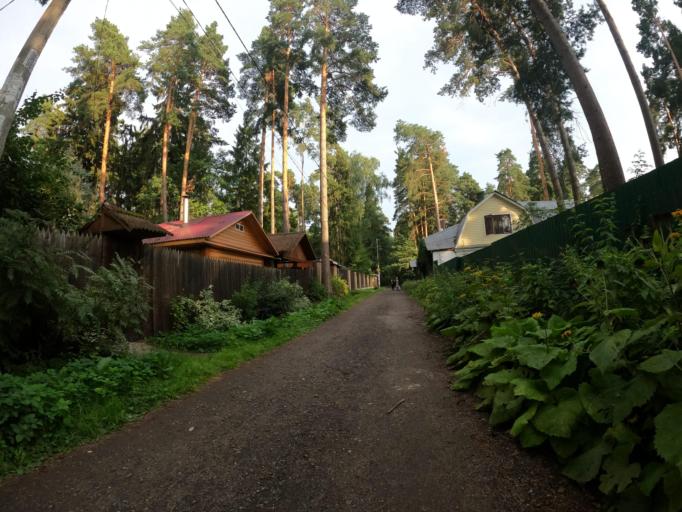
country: RU
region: Moskovskaya
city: Il'inskiy
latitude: 55.6384
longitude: 38.1123
